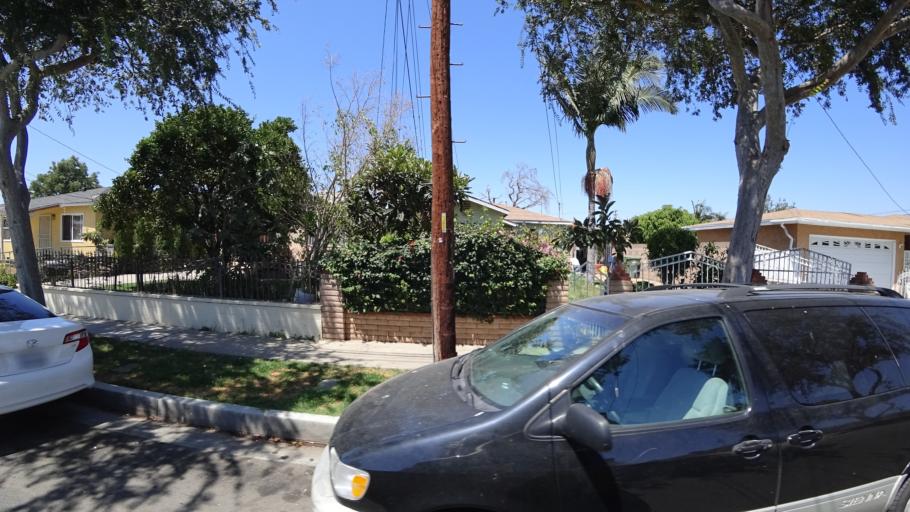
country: US
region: California
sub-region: Los Angeles County
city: Lennox
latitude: 33.9349
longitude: -118.3399
